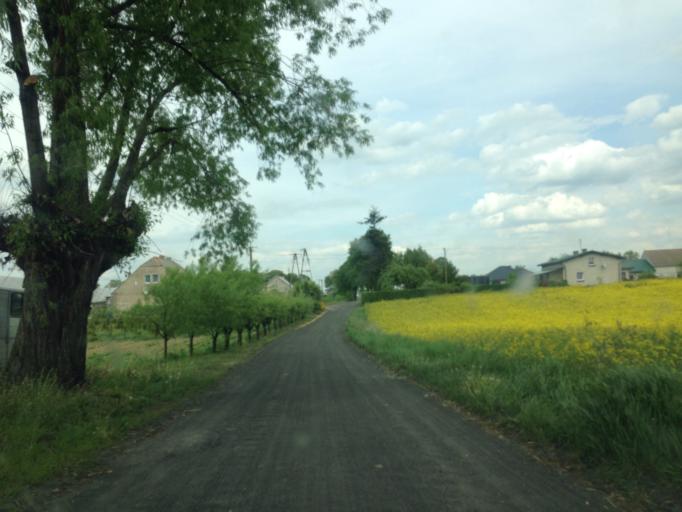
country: PL
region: Kujawsko-Pomorskie
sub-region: Powiat brodnicki
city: Bobrowo
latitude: 53.2733
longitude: 19.3118
